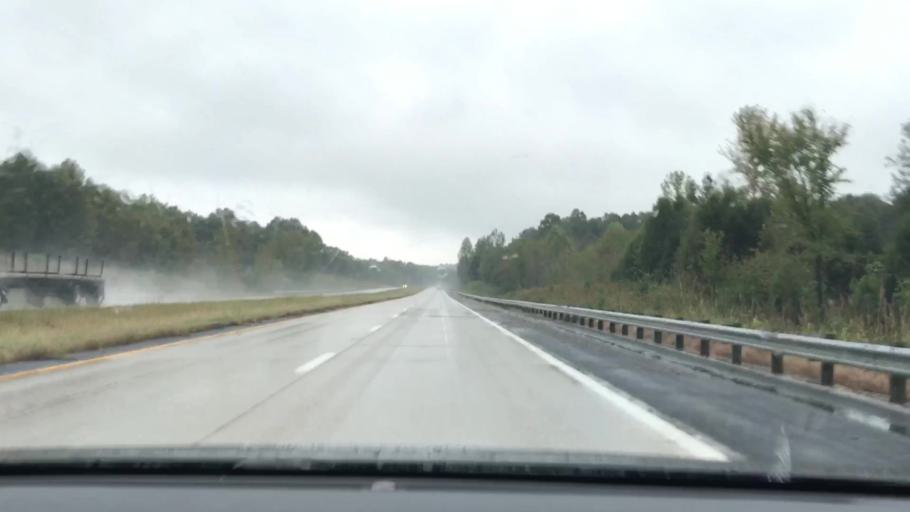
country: US
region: Kentucky
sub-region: Hopkins County
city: Nortonville
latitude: 37.1389
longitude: -87.4613
